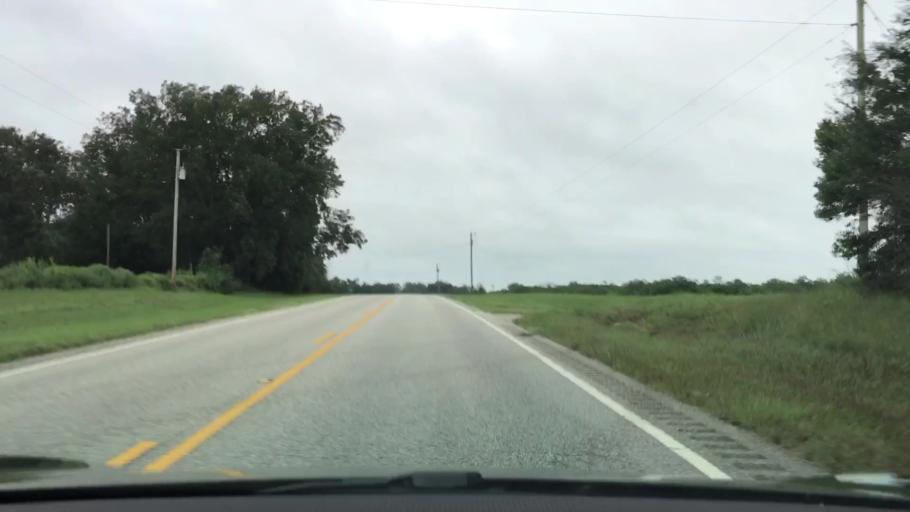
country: US
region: Alabama
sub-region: Coffee County
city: Elba
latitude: 31.3223
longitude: -86.1340
